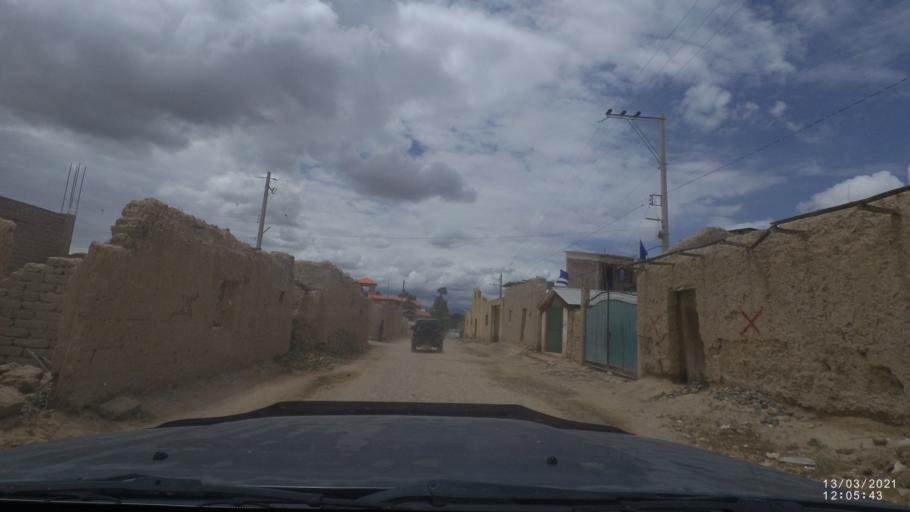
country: BO
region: Cochabamba
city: Tarata
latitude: -17.6291
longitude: -65.9979
